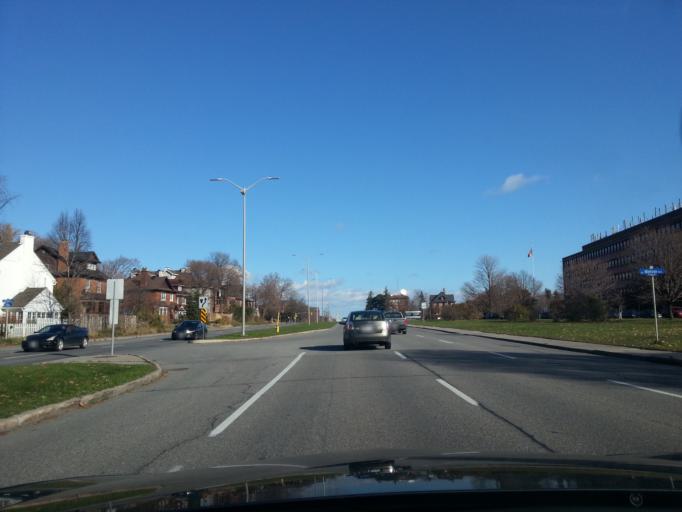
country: CA
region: Ontario
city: Ottawa
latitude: 45.3925
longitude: -75.7190
